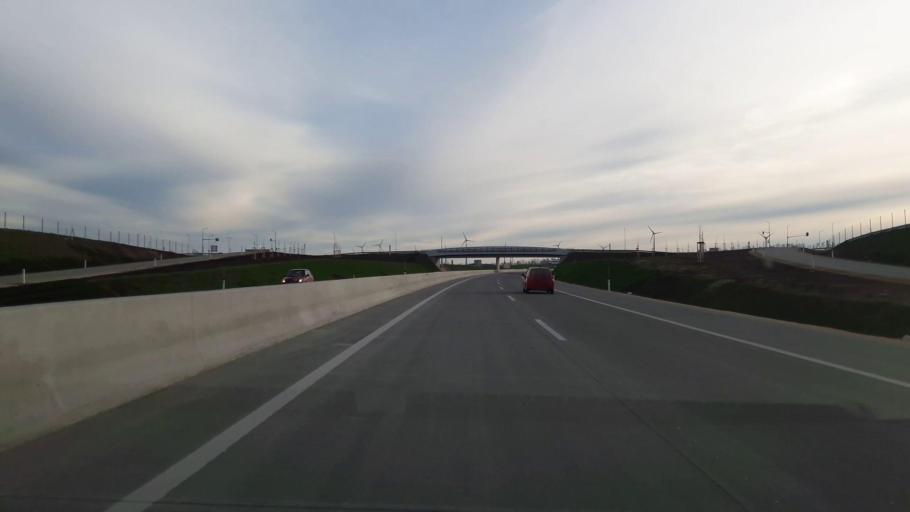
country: AT
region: Lower Austria
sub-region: Politischer Bezirk Mistelbach
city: Wilfersdorf
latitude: 48.5649
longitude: 16.6334
